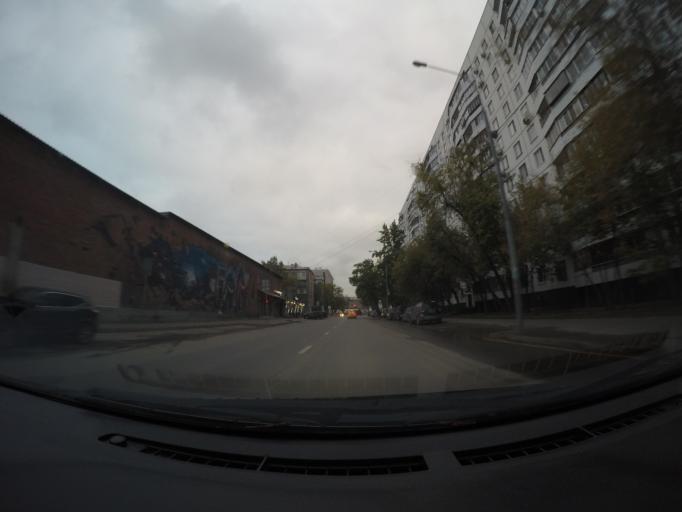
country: RU
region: Moscow
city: Sokol'niki
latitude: 55.7850
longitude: 37.6803
